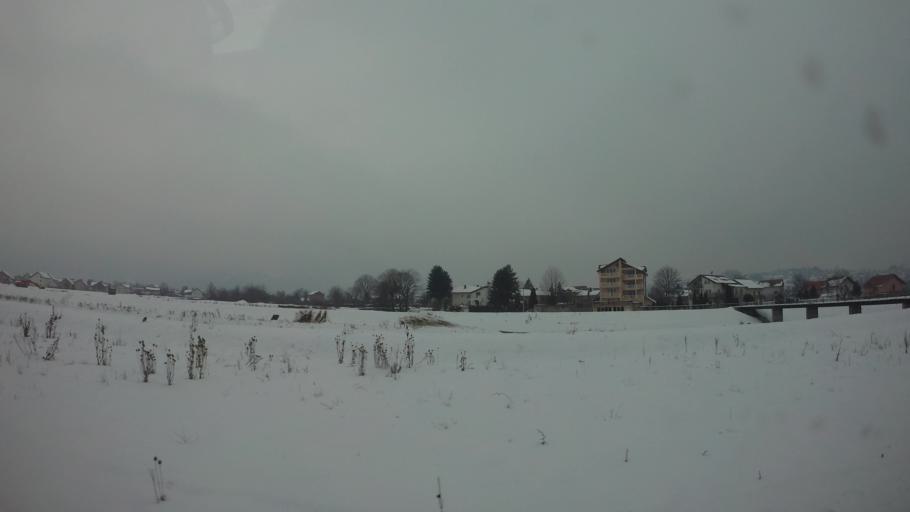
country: BA
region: Federation of Bosnia and Herzegovina
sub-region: Kanton Sarajevo
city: Sarajevo
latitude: 43.8438
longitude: 18.2849
